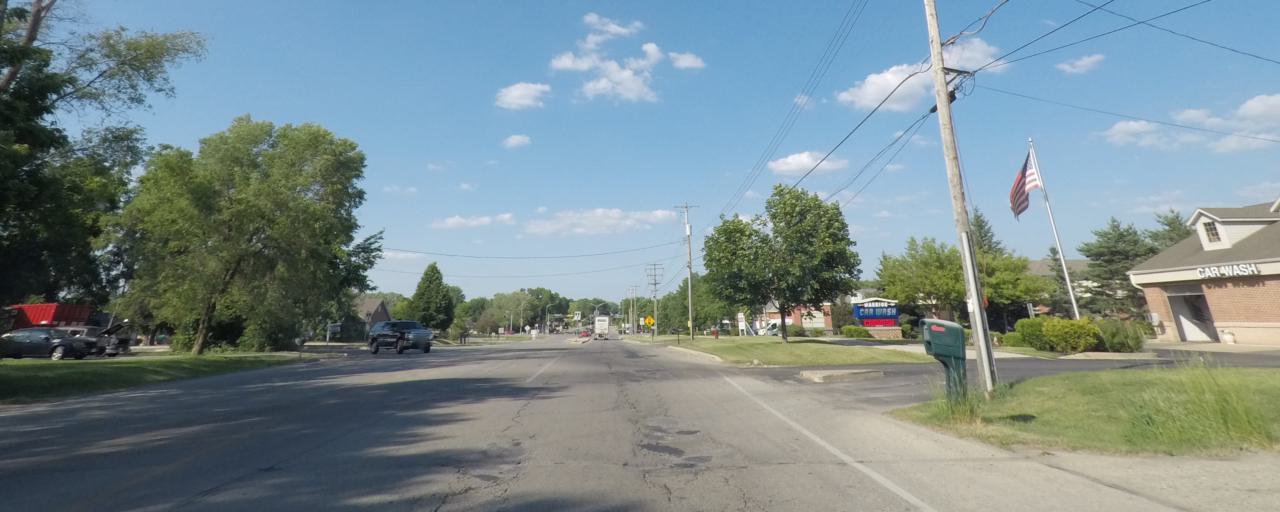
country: US
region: Wisconsin
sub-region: Waukesha County
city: Muskego
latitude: 42.9000
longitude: -88.1513
